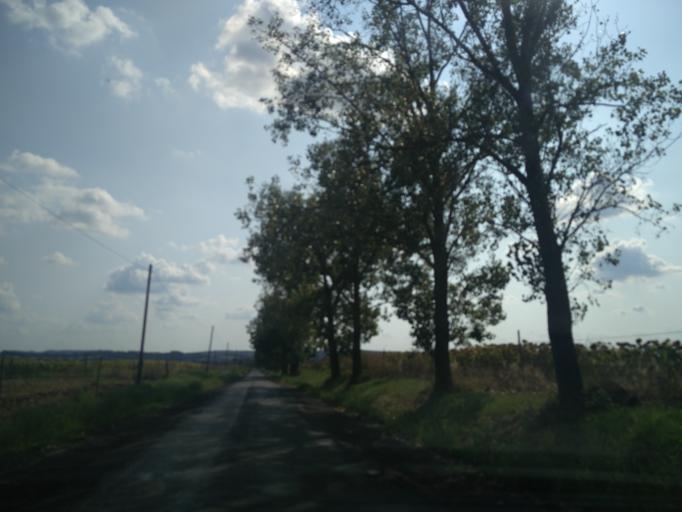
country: HU
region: Zala
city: Zalaegerszeg
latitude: 46.8927
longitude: 16.7601
